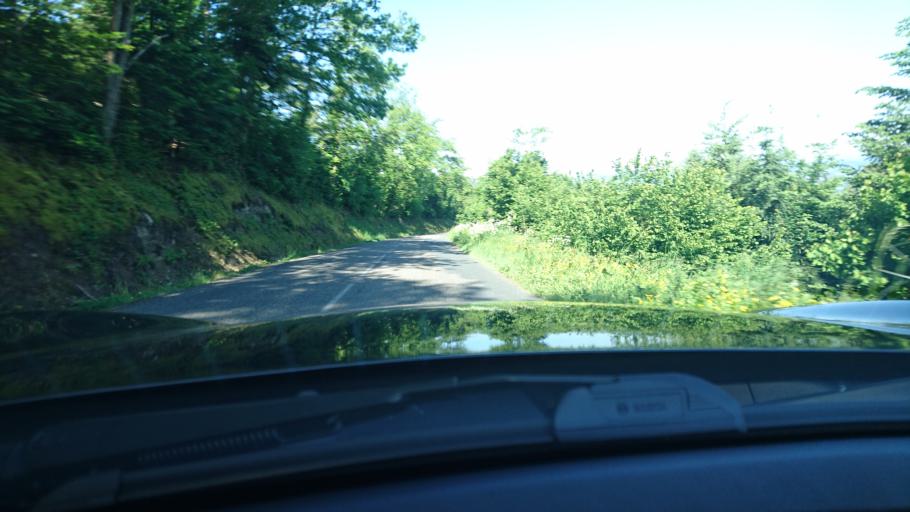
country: FR
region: Rhone-Alpes
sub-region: Departement du Rhone
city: Saint-Pierre-la-Palud
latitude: 45.7608
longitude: 4.6222
